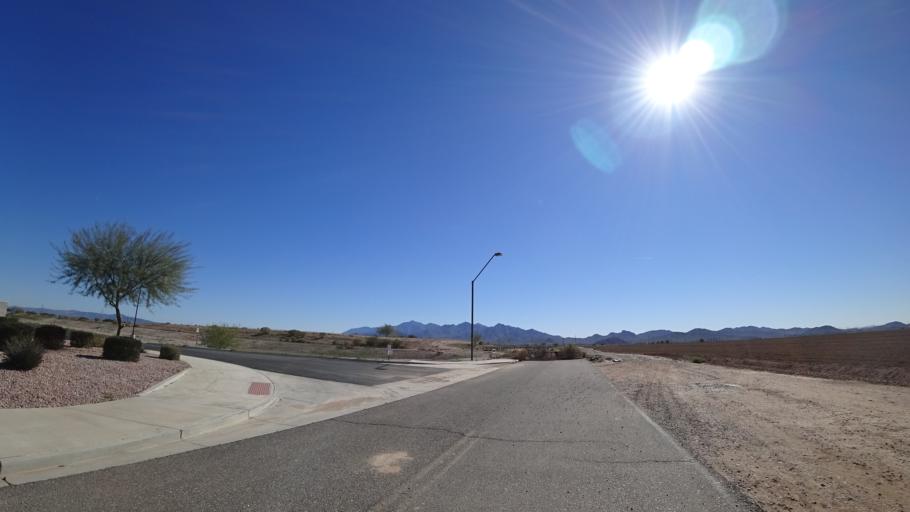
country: US
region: Arizona
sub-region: Maricopa County
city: Goodyear
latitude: 33.4187
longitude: -112.3622
